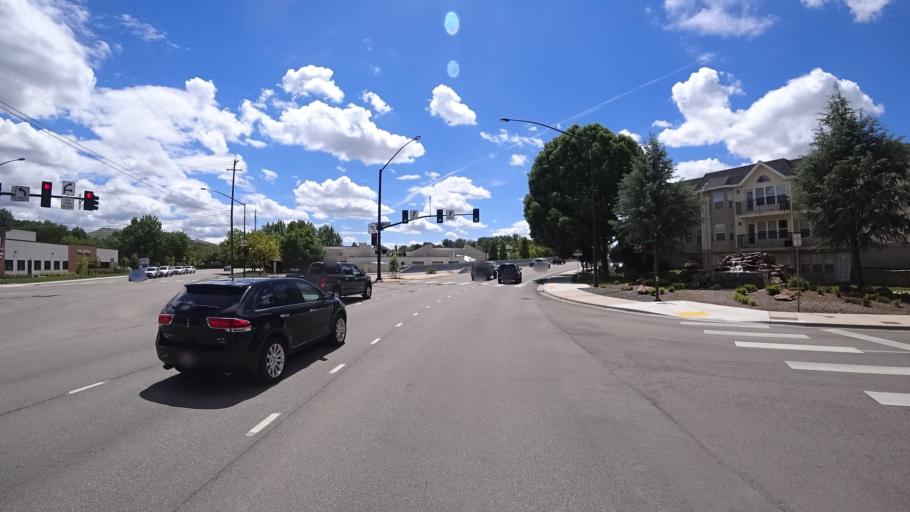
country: US
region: Idaho
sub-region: Ada County
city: Boise
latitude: 43.6030
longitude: -116.1888
